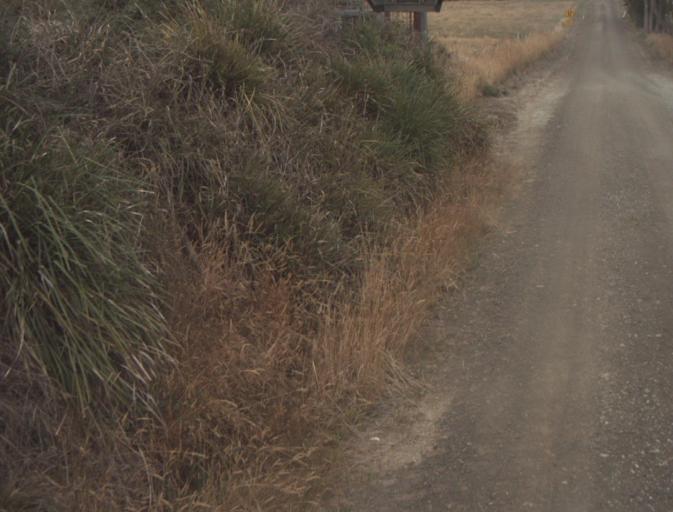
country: AU
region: Tasmania
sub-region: Launceston
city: Mayfield
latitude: -41.2106
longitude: 147.1496
